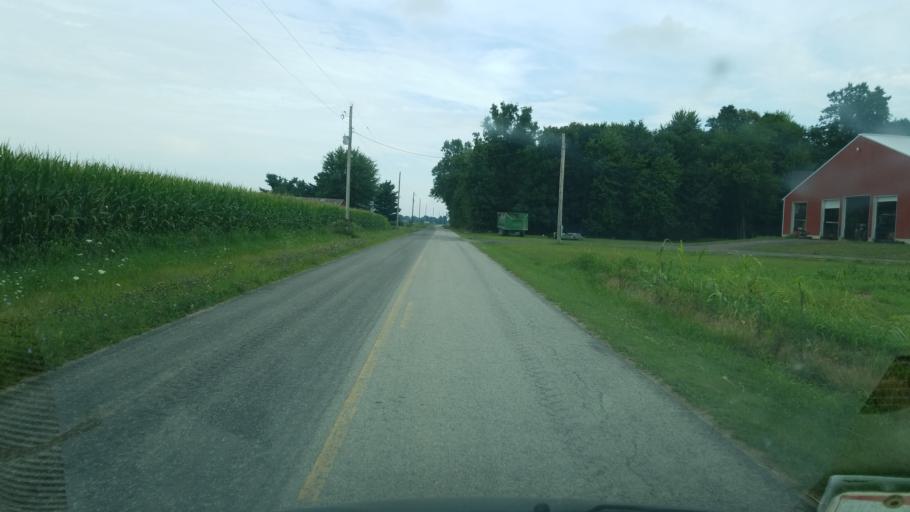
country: US
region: Ohio
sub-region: Seneca County
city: Tiffin
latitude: 40.9979
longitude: -83.0550
